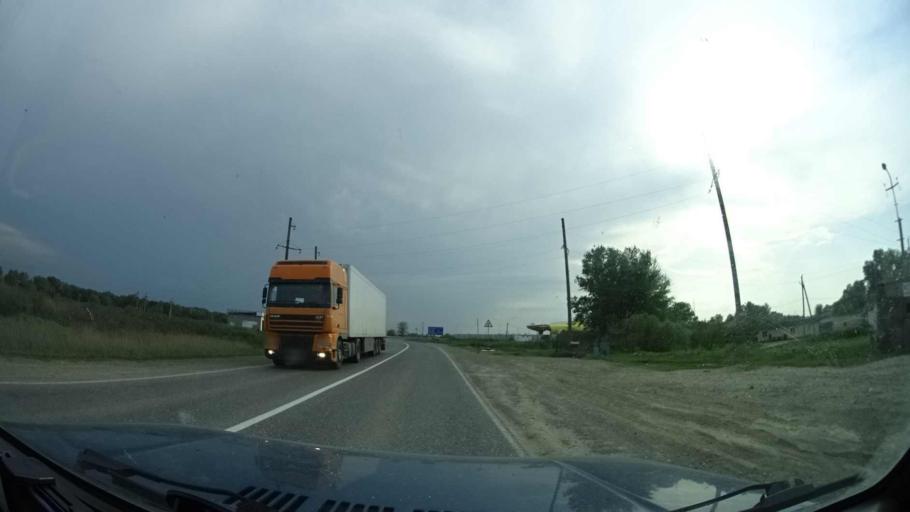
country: RU
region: Dagestan
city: Babayurt
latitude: 43.5752
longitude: 46.7376
